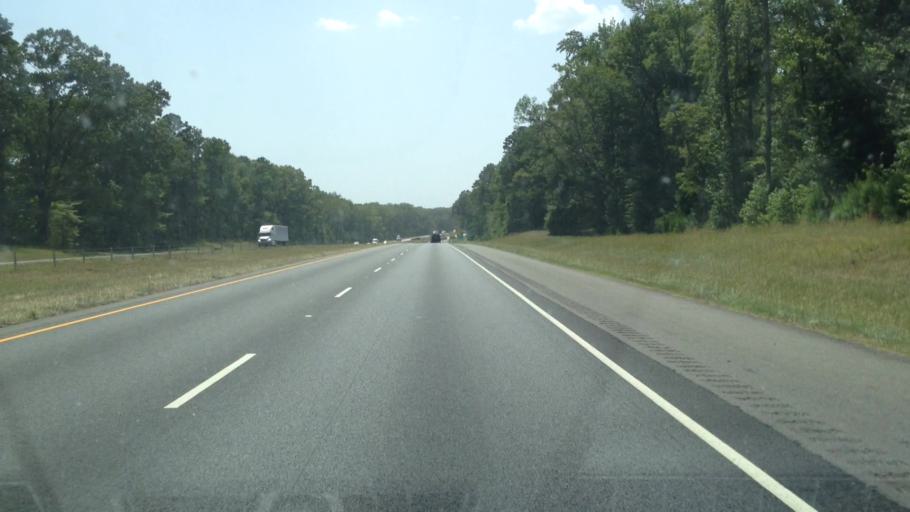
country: US
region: Louisiana
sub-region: Webster Parish
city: Minden
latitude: 32.5620
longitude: -93.1413
